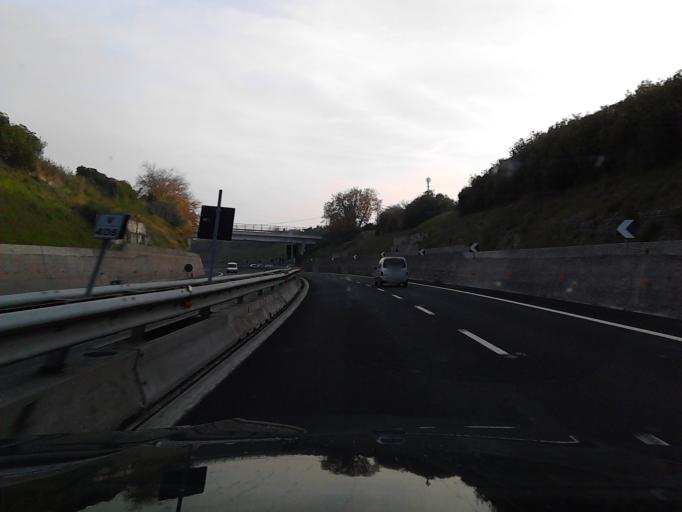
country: IT
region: Abruzzo
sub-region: Provincia di Chieti
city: San Vito Chietino
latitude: 42.3041
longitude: 14.4221
